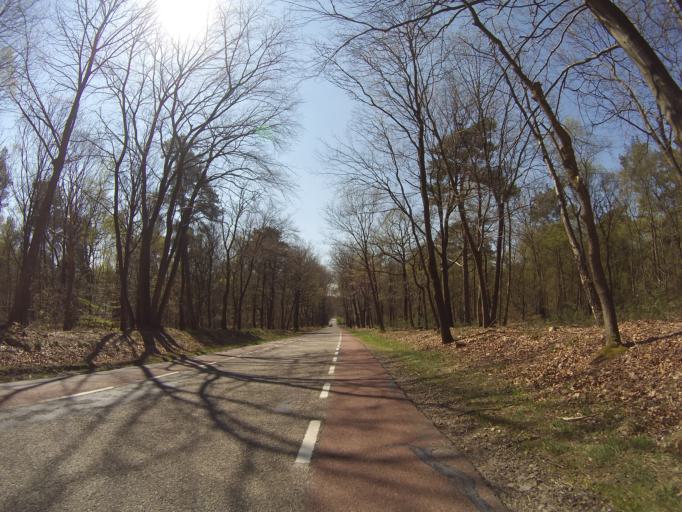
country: NL
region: Utrecht
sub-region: Gemeente Utrechtse Heuvelrug
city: Amerongen
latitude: 52.0145
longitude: 5.4721
